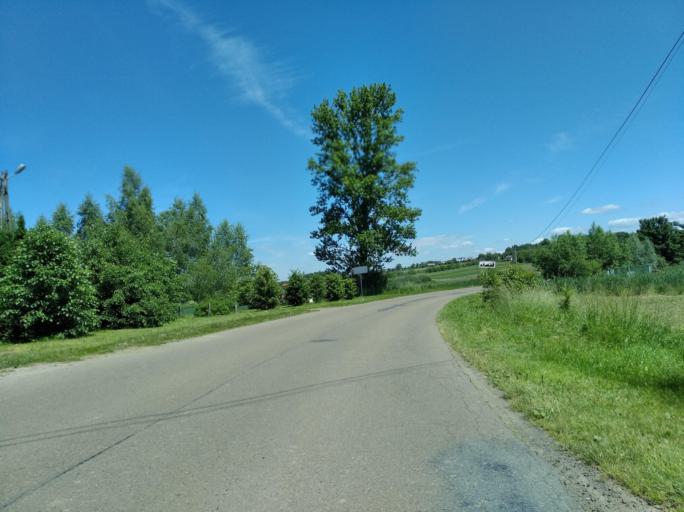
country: PL
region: Subcarpathian Voivodeship
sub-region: Powiat jasielski
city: Tarnowiec
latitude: 49.7256
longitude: 21.5650
